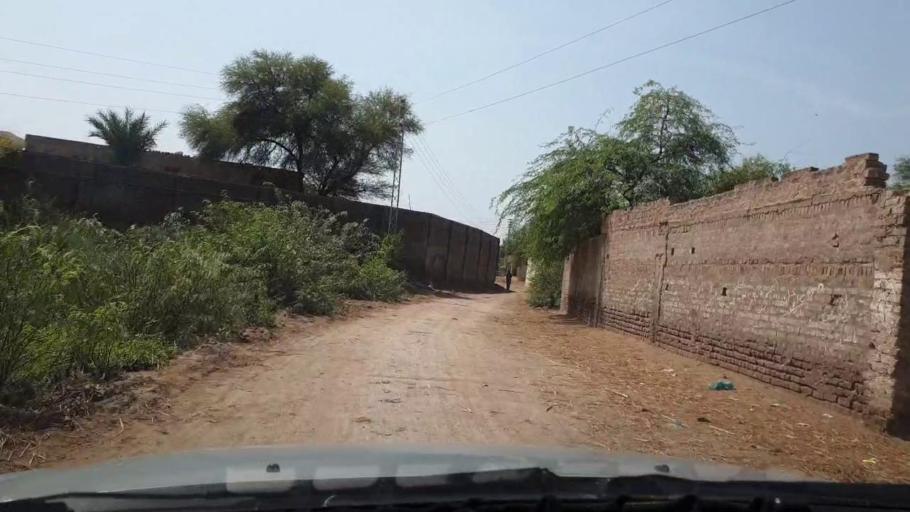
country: PK
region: Sindh
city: Tando Muhammad Khan
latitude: 25.1226
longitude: 68.6205
